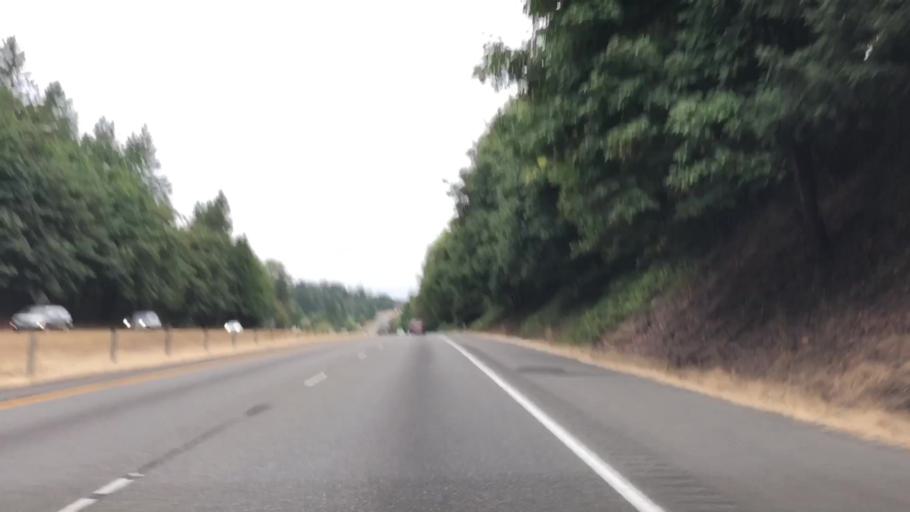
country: US
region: Washington
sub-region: Pierce County
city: Gig Harbor
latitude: 47.3256
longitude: -122.5942
